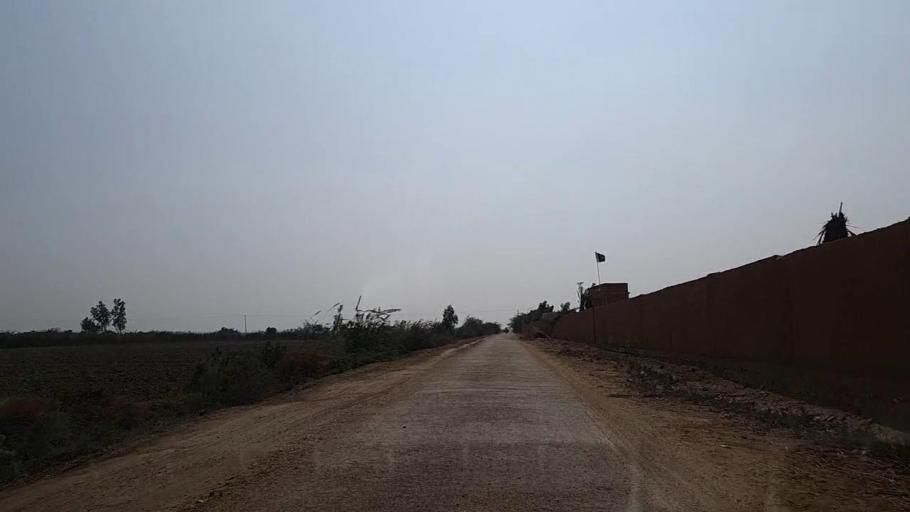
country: PK
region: Sindh
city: Thatta
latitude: 24.7079
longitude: 67.7673
